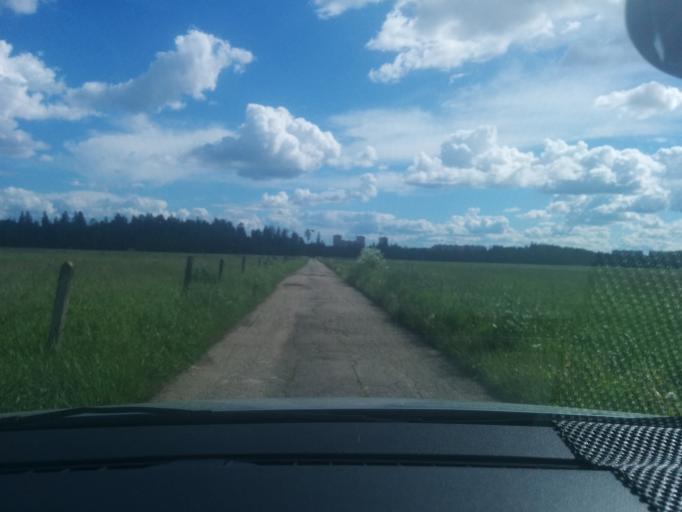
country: RU
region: Moskovskaya
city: Lugovaya
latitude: 56.0431
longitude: 37.4974
